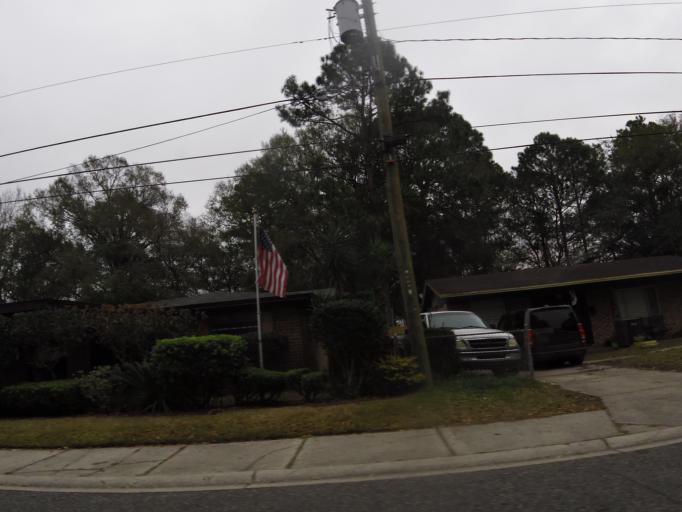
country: US
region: Florida
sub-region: Duval County
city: Jacksonville
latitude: 30.3593
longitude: -81.6987
